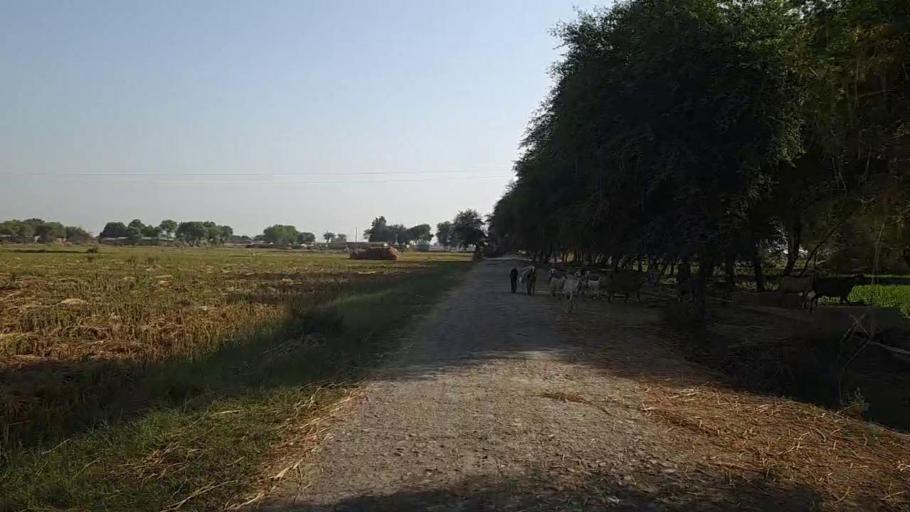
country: PK
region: Sindh
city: Kandhkot
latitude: 28.3535
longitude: 69.3351
